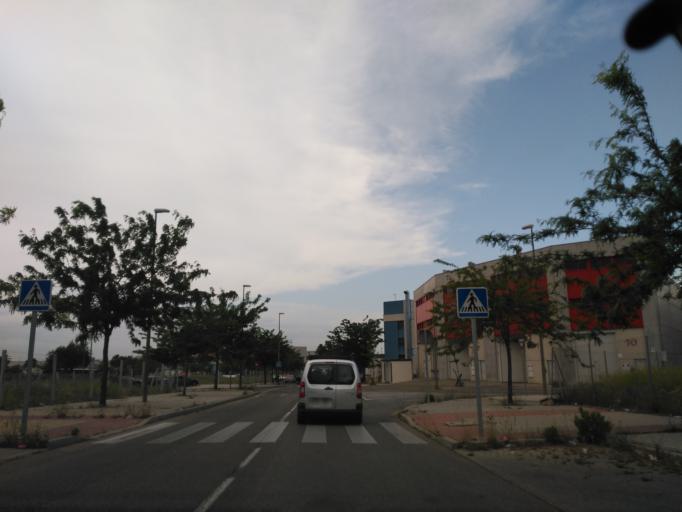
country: ES
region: Madrid
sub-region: Provincia de Madrid
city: Villaverde
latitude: 40.3348
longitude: -3.7173
